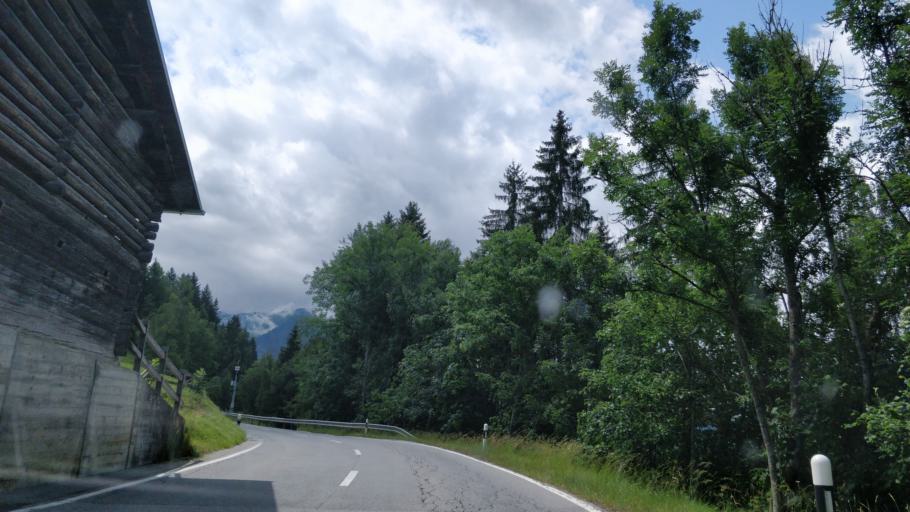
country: CH
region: Grisons
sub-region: Surselva District
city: Ilanz
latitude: 46.7099
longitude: 9.1942
